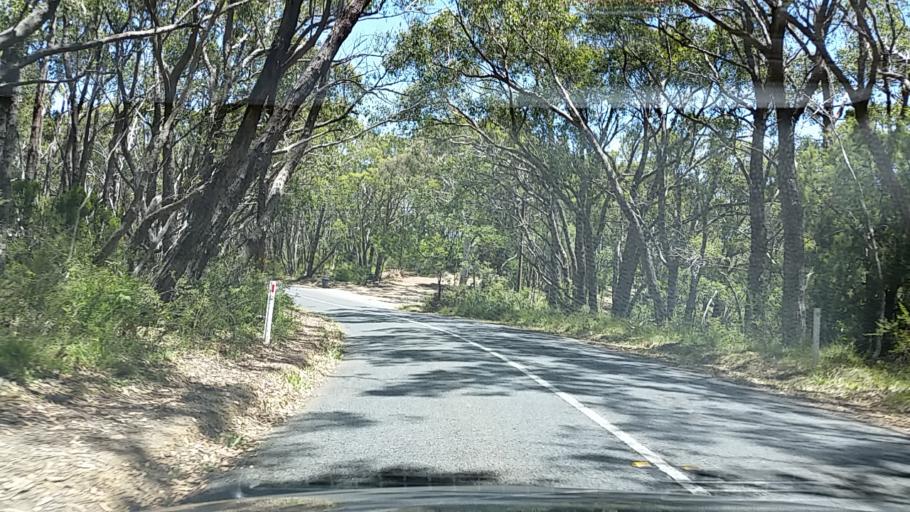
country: AU
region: South Australia
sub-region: Adelaide Hills
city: Crafers
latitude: -34.9939
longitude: 138.6925
